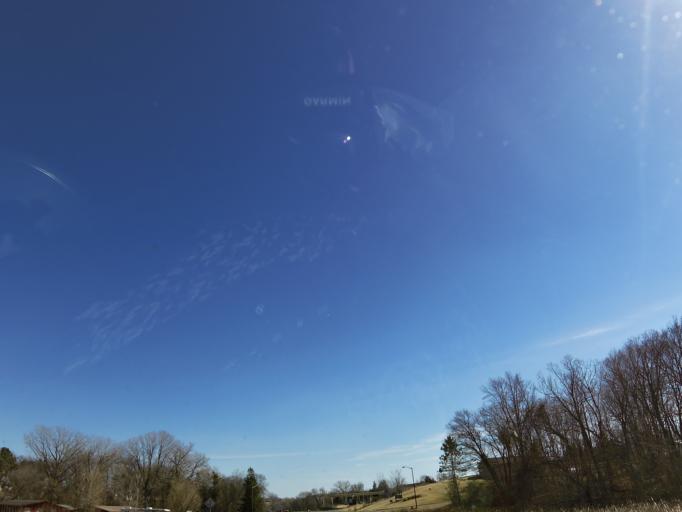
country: US
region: Minnesota
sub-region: Wright County
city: Rockford
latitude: 45.0912
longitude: -93.7439
